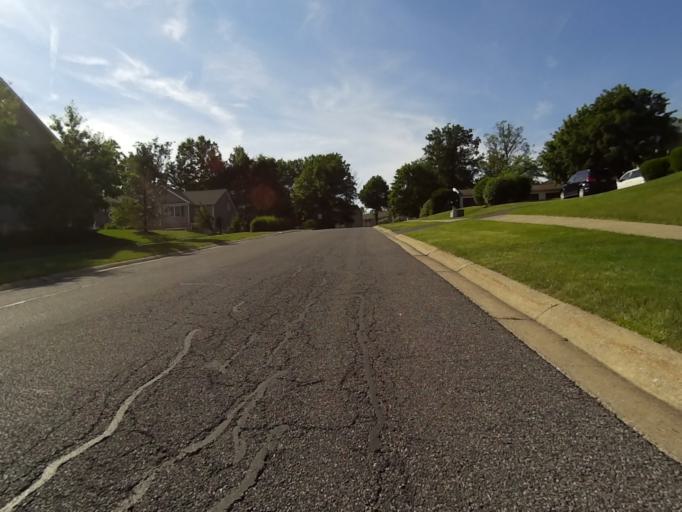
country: US
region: Pennsylvania
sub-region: Centre County
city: Park Forest Village
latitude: 40.8058
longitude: -77.9245
